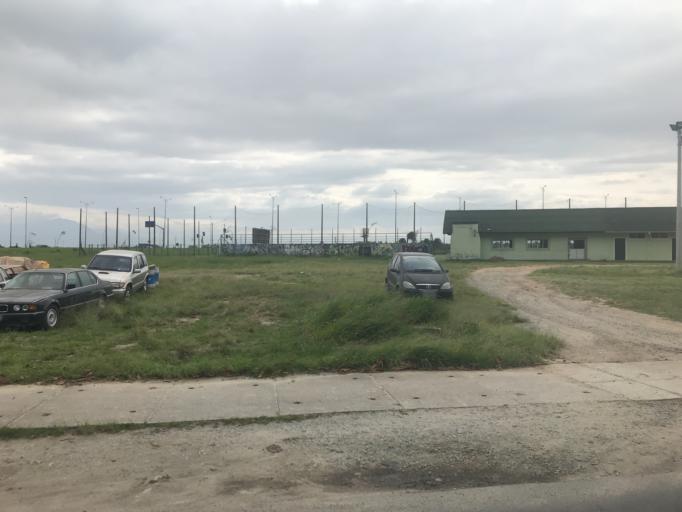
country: BR
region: Santa Catarina
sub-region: Florianopolis
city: Costeira do Pirajubae
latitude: -27.6279
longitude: -48.5246
